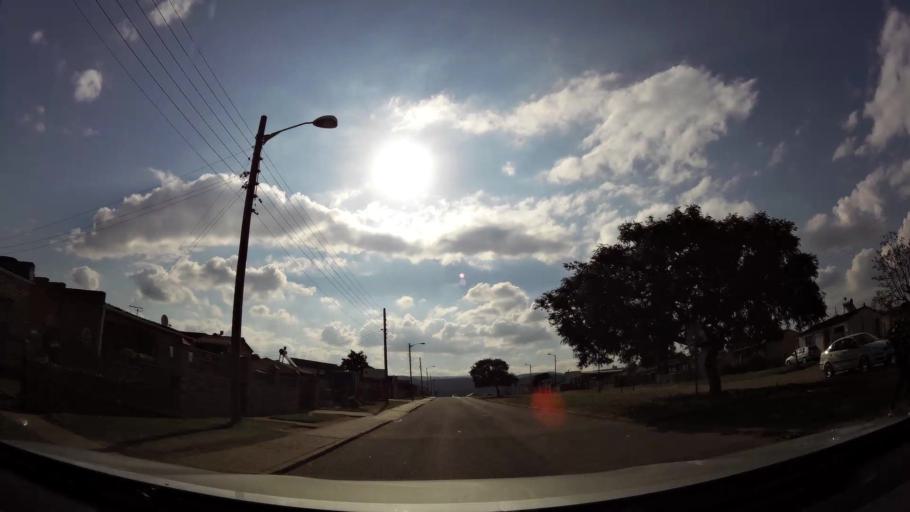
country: ZA
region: Eastern Cape
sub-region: Nelson Mandela Bay Metropolitan Municipality
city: Uitenhage
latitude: -33.7376
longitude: 25.3709
